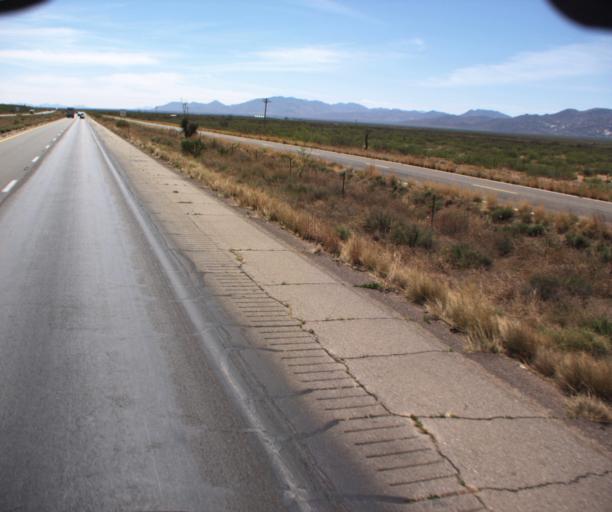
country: US
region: Arizona
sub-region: Cochise County
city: Willcox
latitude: 32.3270
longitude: -109.5094
